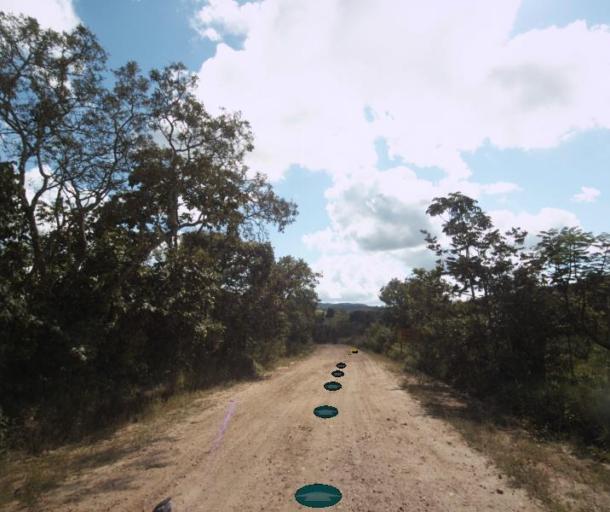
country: BR
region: Goias
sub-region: Pirenopolis
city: Pirenopolis
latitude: -15.7941
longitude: -49.0863
